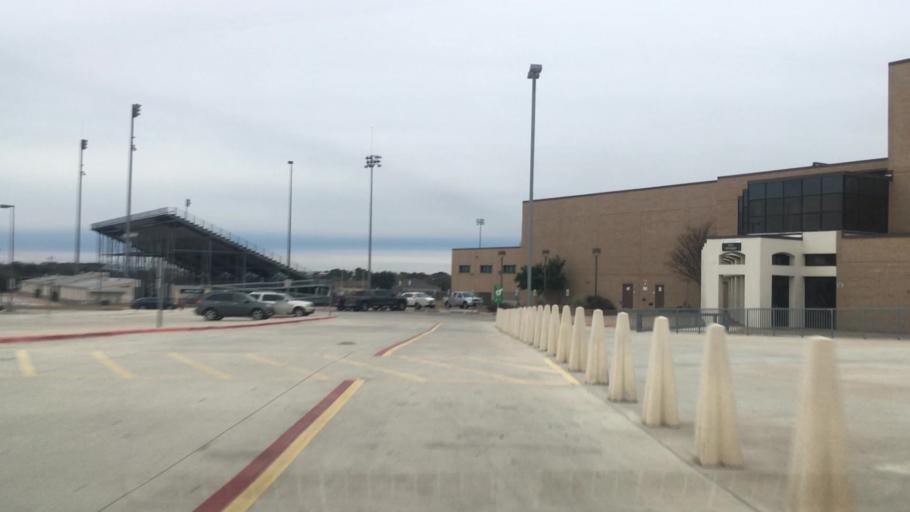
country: US
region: Texas
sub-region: Williamson County
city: Leander
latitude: 30.5386
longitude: -97.8503
